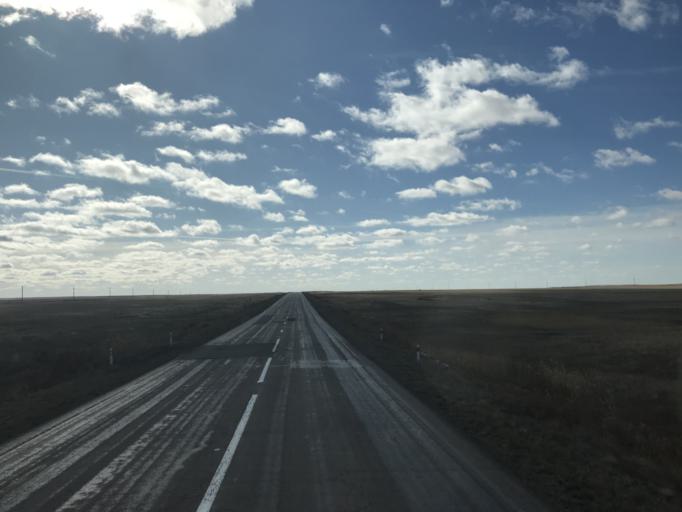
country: RU
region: Orenburg
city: Yasnyy
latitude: 50.4675
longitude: 60.1612
